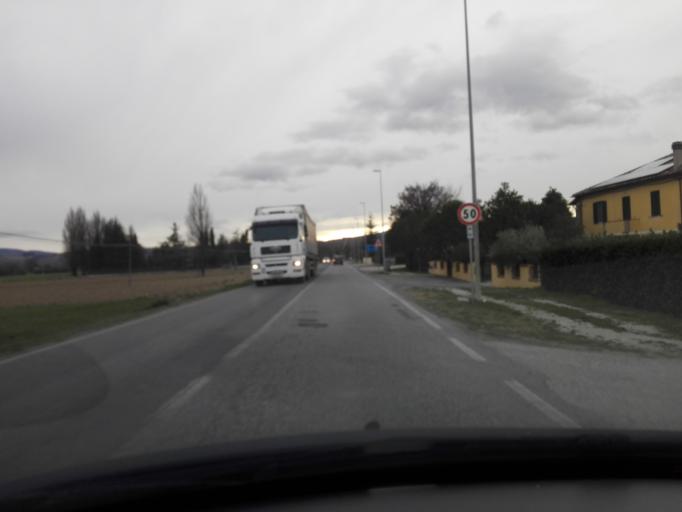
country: IT
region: Umbria
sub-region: Provincia di Perugia
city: Bevagna
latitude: 42.9482
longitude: 12.6486
